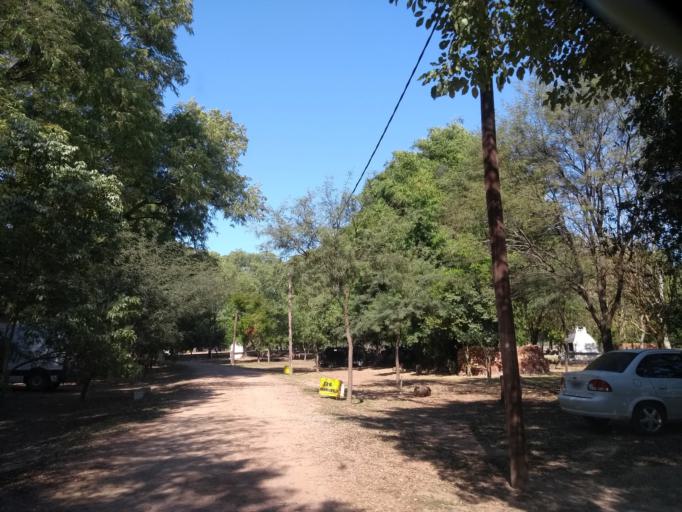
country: AR
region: Chaco
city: Presidencia Roque Saenz Pena
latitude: -26.8207
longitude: -60.4194
